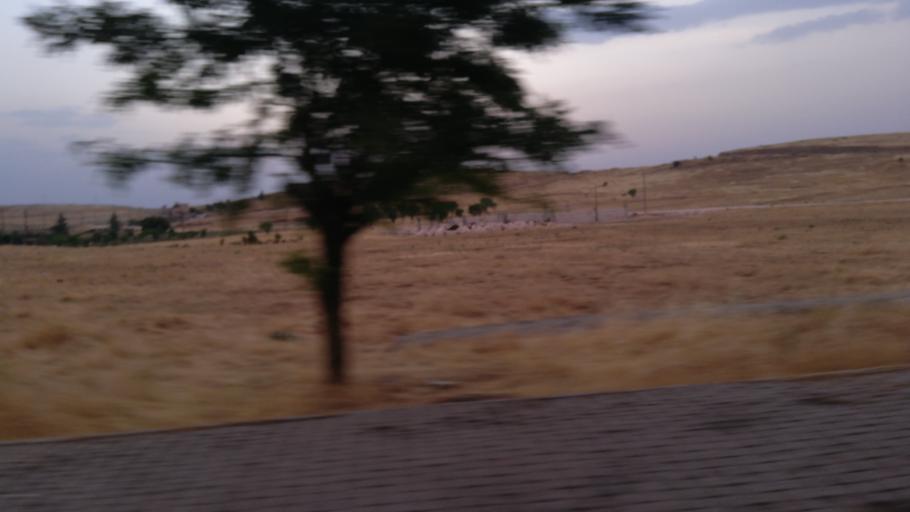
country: TR
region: Mardin
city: Kindirip
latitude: 37.4612
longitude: 41.2253
